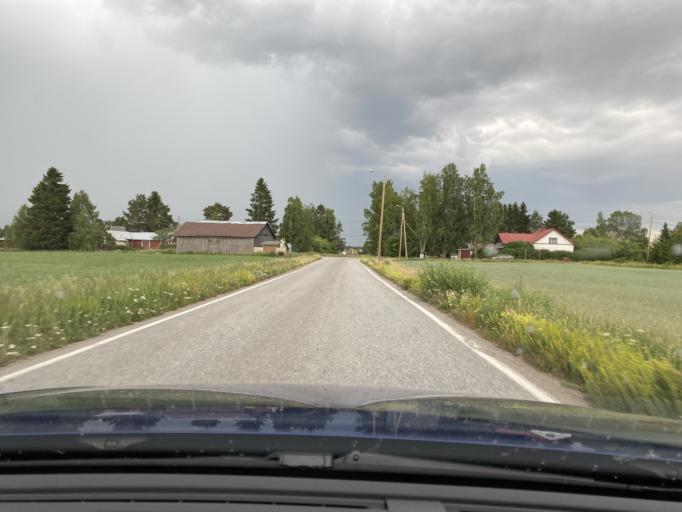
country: FI
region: Satakunta
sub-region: Rauma
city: Eura
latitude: 61.1579
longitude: 22.1056
